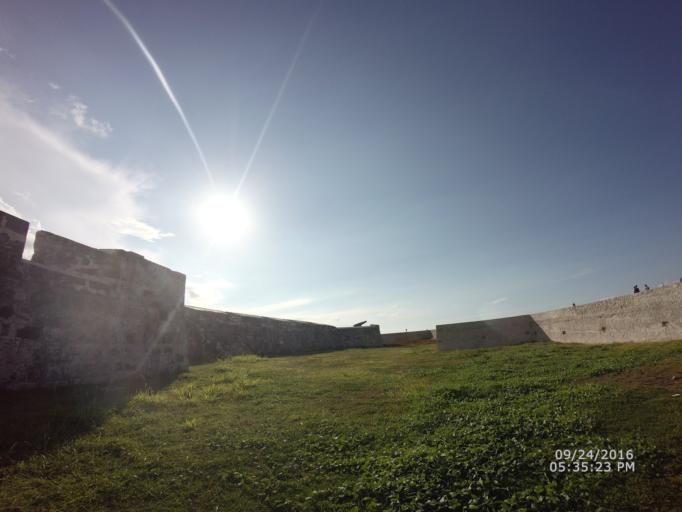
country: CU
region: La Habana
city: Centro Habana
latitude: 23.1463
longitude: -82.3571
